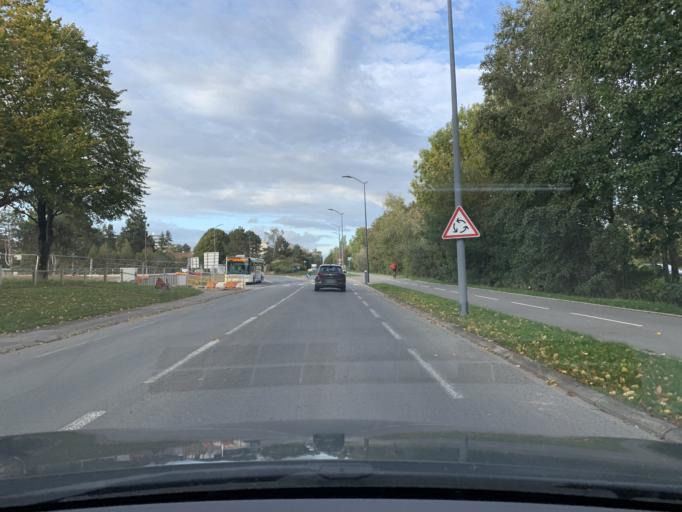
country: FR
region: Picardie
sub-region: Departement de l'Aisne
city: Harly
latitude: 49.8532
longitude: 3.3104
